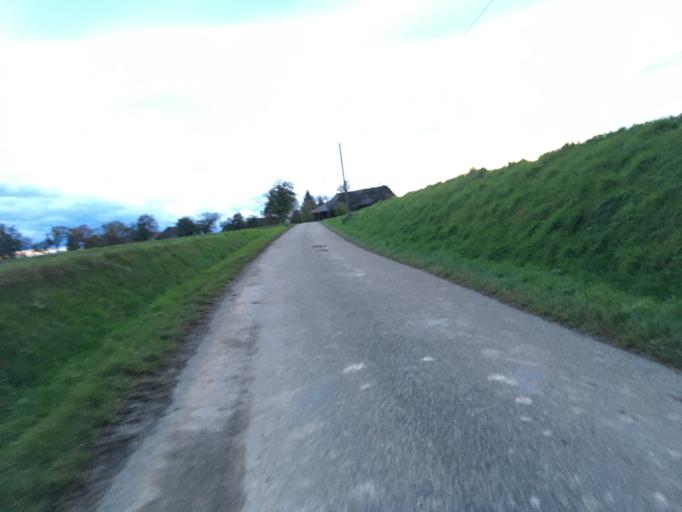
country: DE
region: Baden-Wuerttemberg
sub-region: Karlsruhe Region
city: Osterburken
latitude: 49.3915
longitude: 9.4535
